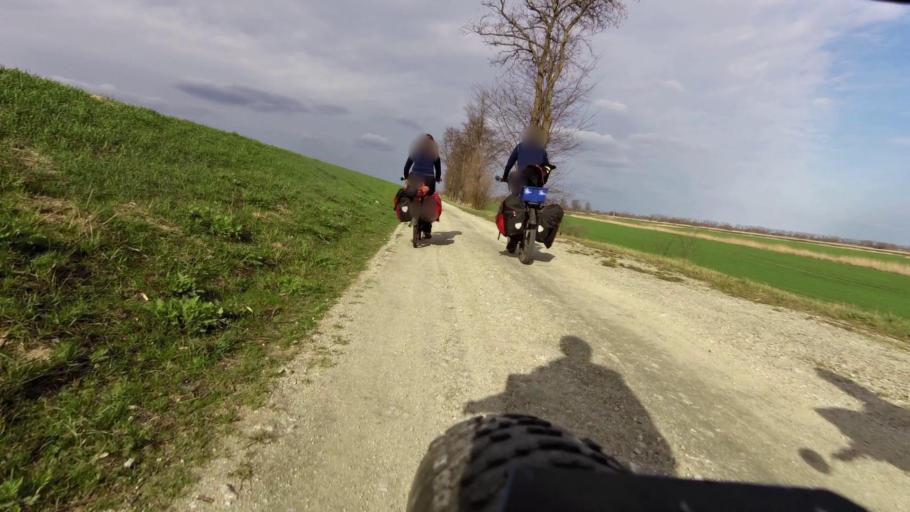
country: PL
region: Lubusz
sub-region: Powiat gorzowski
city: Kostrzyn nad Odra
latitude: 52.5553
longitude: 14.6256
